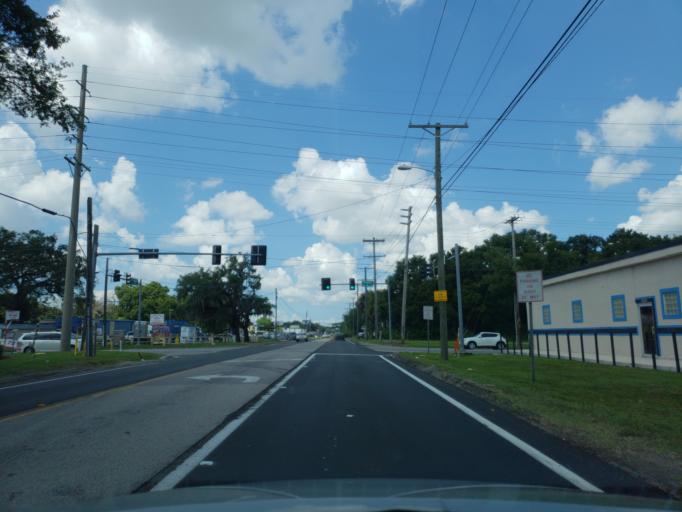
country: US
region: Florida
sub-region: Hillsborough County
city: East Lake-Orient Park
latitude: 27.9668
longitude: -82.3726
